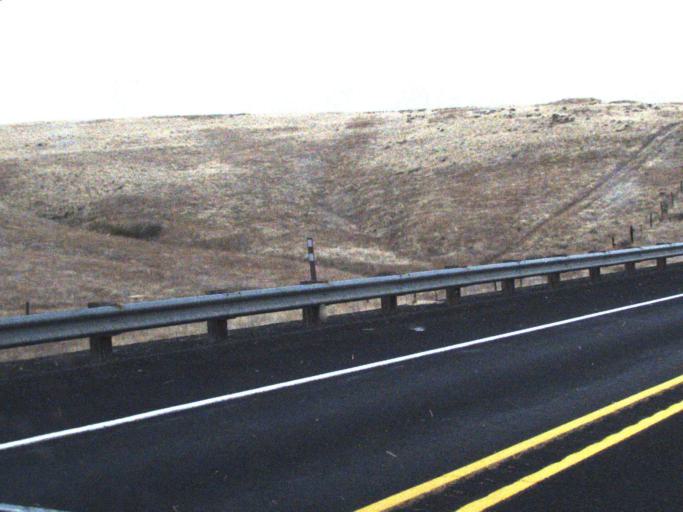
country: US
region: Washington
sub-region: Columbia County
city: Dayton
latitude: 46.7659
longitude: -118.0040
